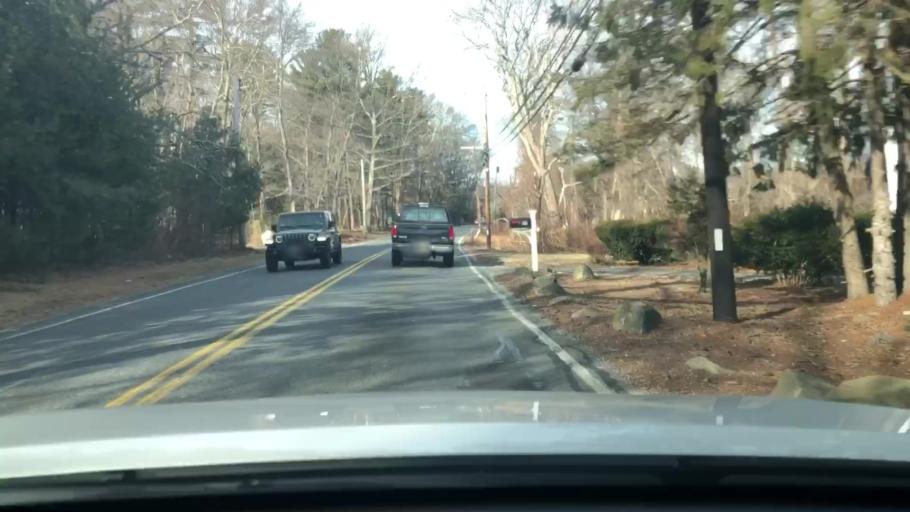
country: US
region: Massachusetts
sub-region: Worcester County
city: Mendon
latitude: 42.0912
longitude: -71.5346
